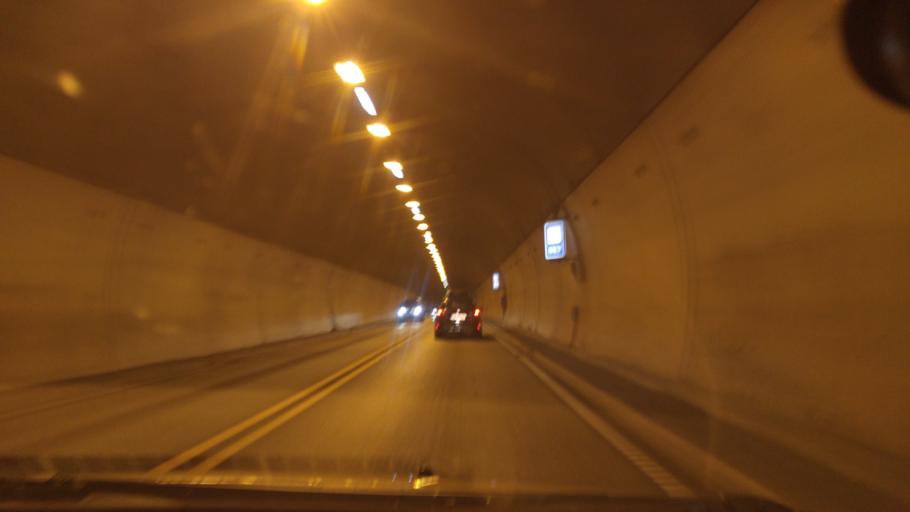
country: NO
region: Sor-Trondelag
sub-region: Malvik
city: Malvik
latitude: 63.4229
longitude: 10.5852
